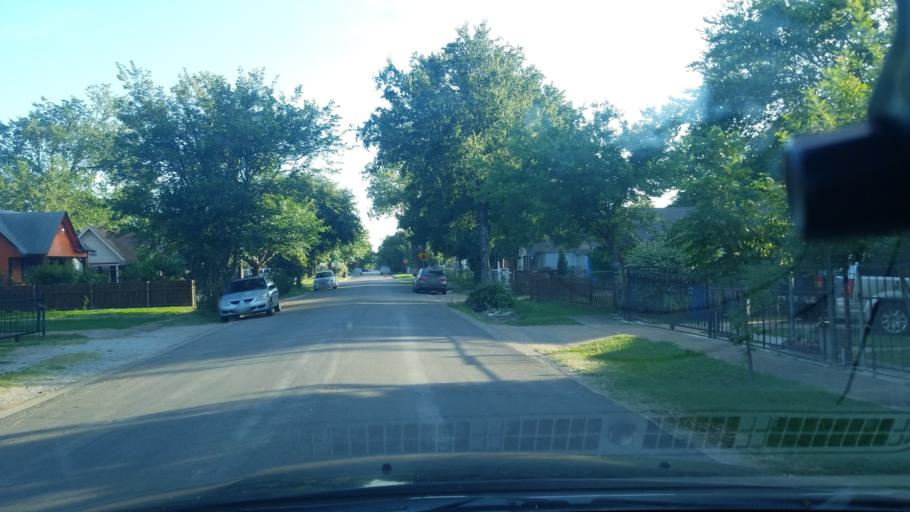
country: US
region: Texas
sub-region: Dallas County
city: Dallas
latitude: 32.7182
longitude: -96.8217
